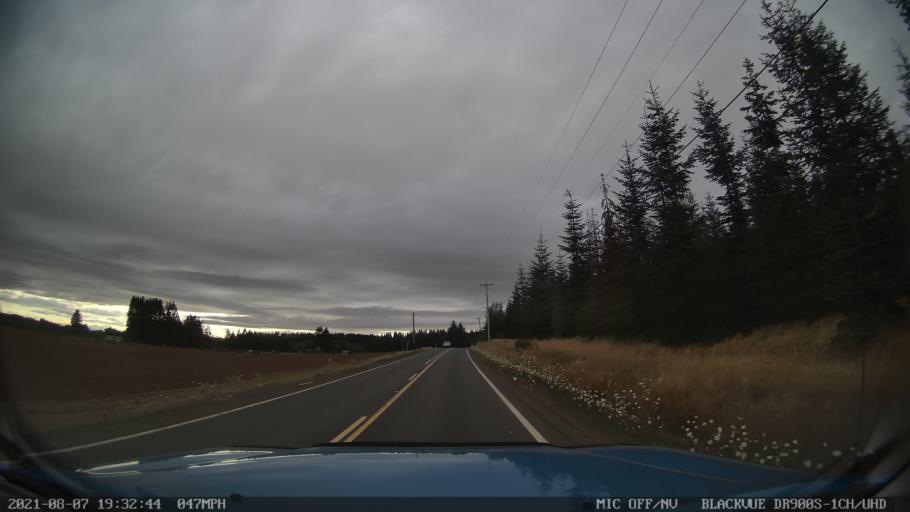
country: US
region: Oregon
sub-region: Linn County
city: Lyons
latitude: 44.9023
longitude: -122.6473
